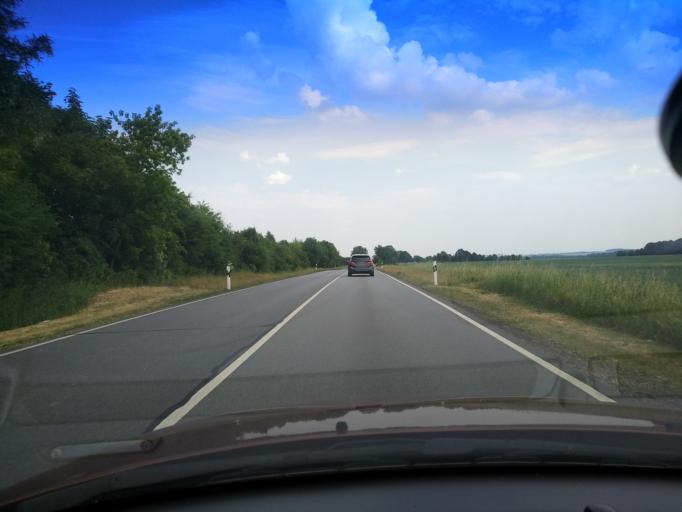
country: DE
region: Saxony
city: Niesky
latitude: 51.2675
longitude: 14.8515
